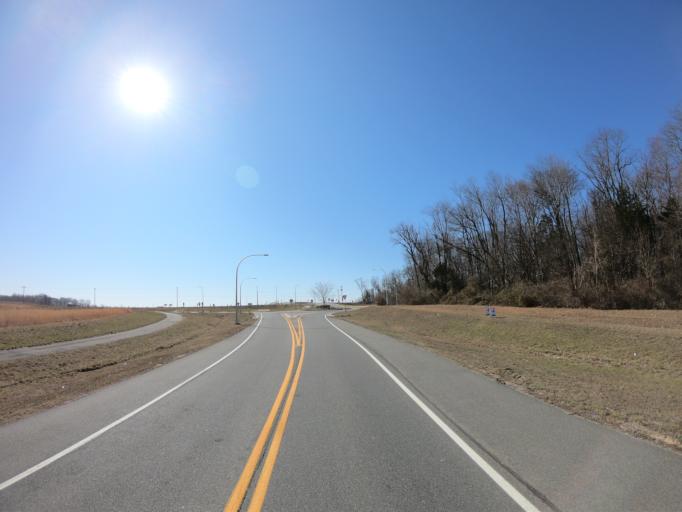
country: US
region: Delaware
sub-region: New Castle County
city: Middletown
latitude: 39.5280
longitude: -75.6792
